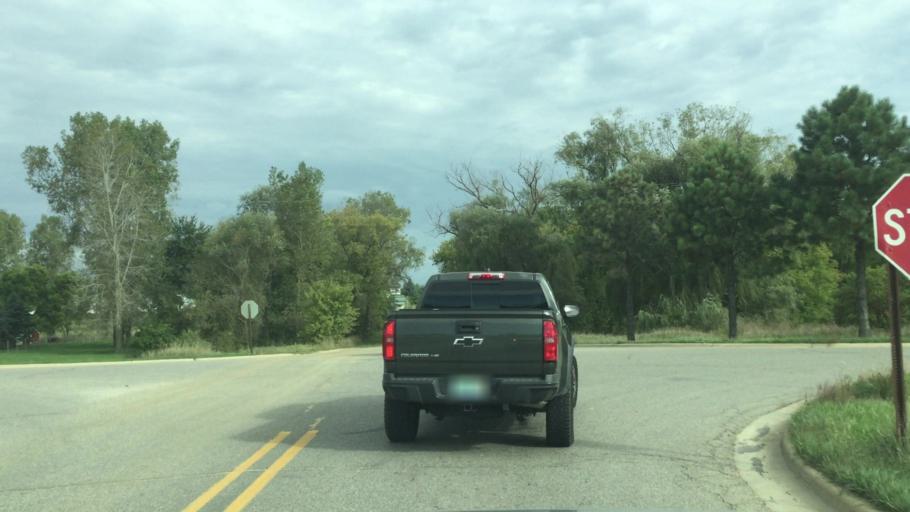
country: US
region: Michigan
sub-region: Genesee County
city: Argentine
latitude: 42.7036
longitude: -83.8798
